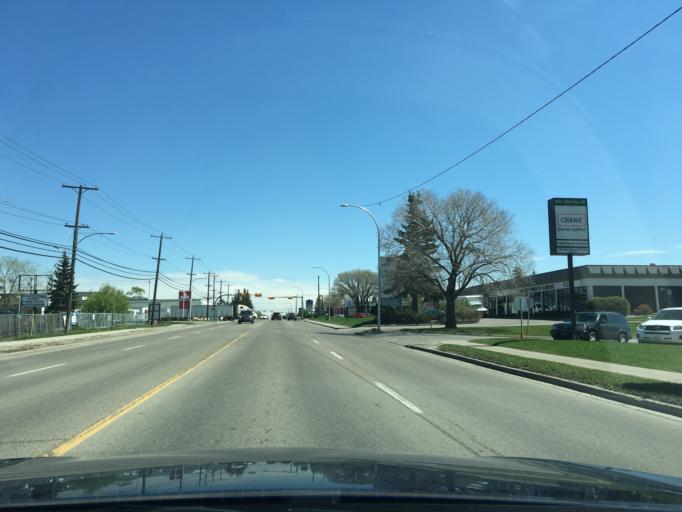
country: CA
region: Alberta
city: Calgary
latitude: 51.0014
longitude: -114.0592
